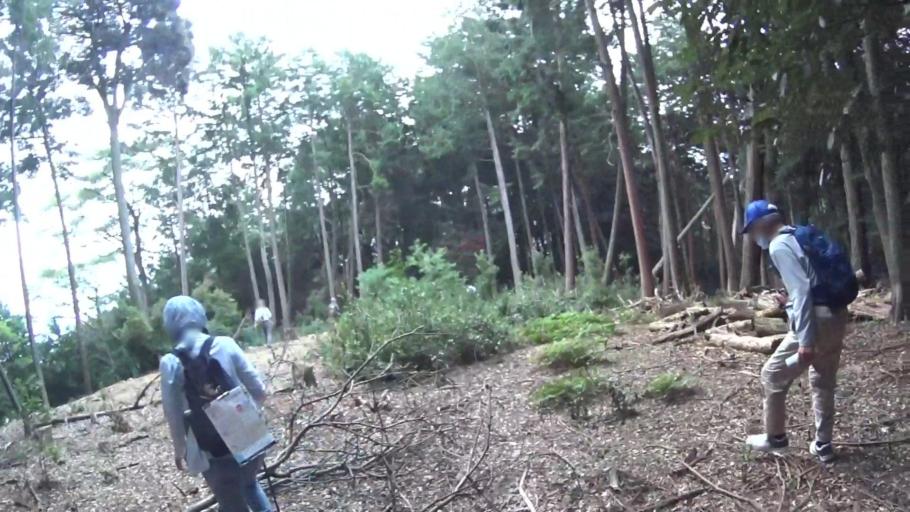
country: JP
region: Shiga Prefecture
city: Hikone
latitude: 35.2826
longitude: 136.3984
